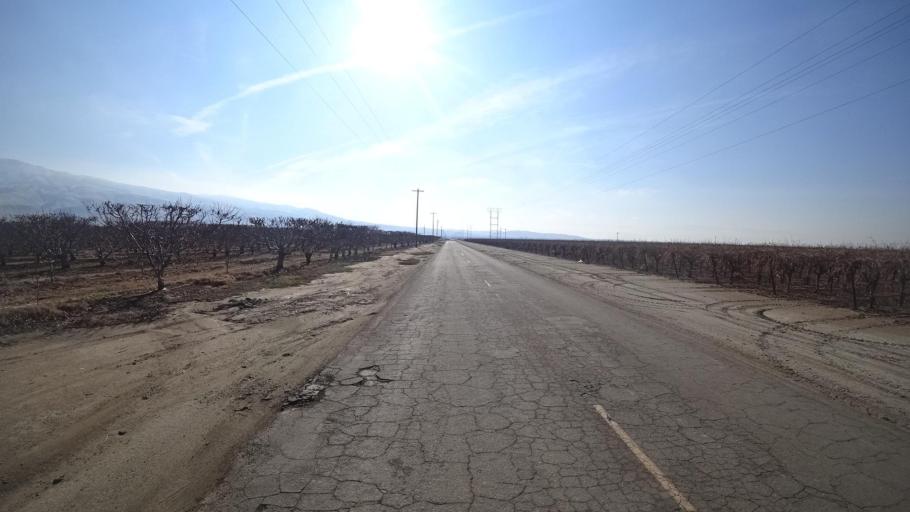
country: US
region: California
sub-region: Kern County
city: Arvin
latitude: 35.1973
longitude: -118.8061
